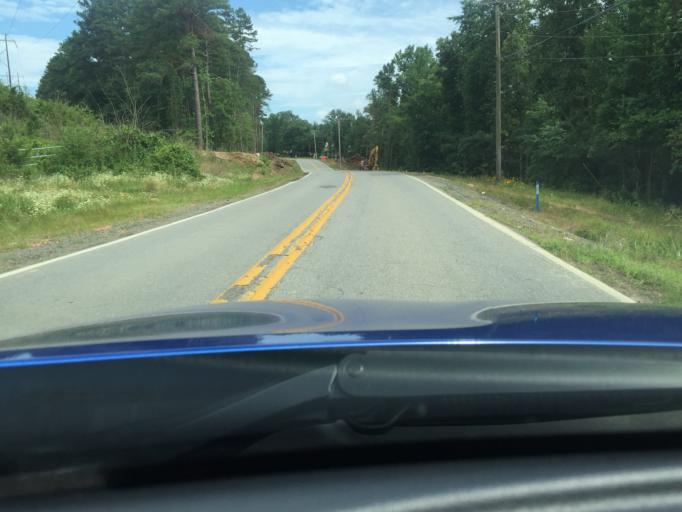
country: US
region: Arkansas
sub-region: Pulaski County
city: Maumelle
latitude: 34.8101
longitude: -92.4424
